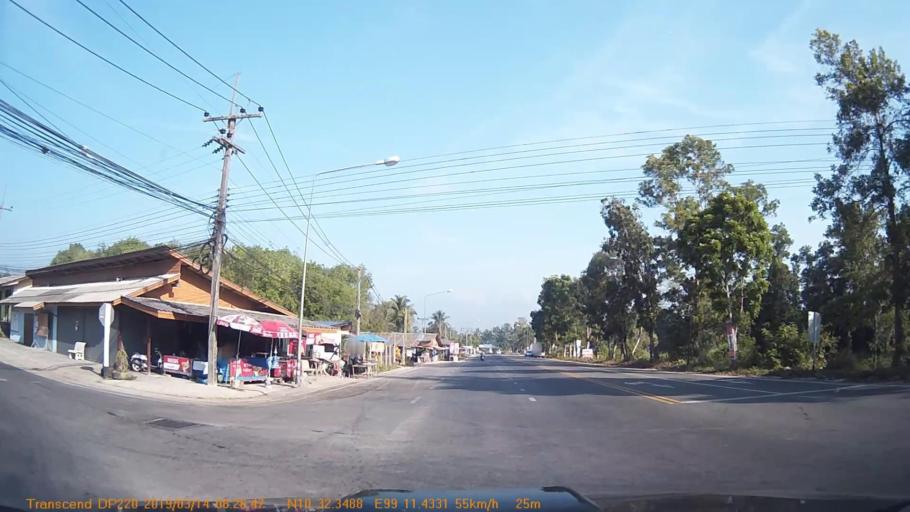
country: TH
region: Chumphon
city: Chumphon
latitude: 10.5393
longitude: 99.1904
